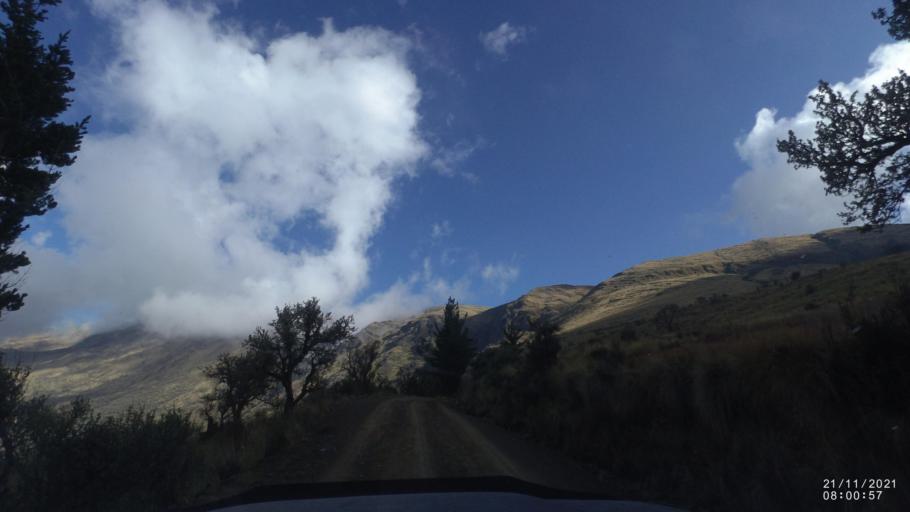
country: BO
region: Cochabamba
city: Cochabamba
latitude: -17.2899
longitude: -66.2197
